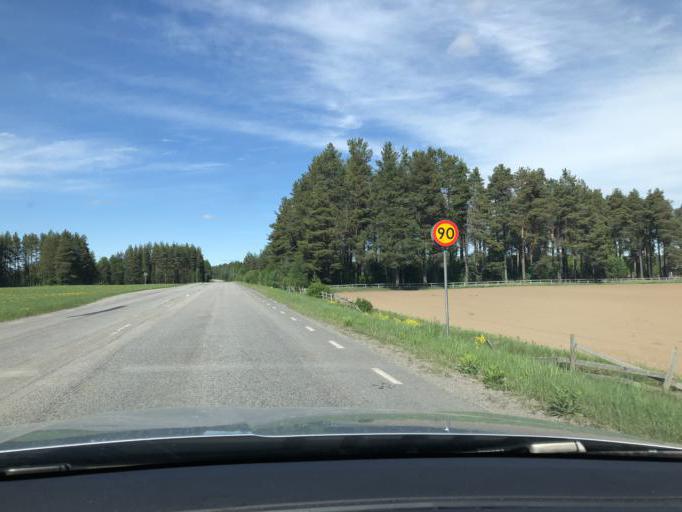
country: SE
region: Norrbotten
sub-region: Pitea Kommun
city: Bergsviken
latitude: 65.3558
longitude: 21.3818
